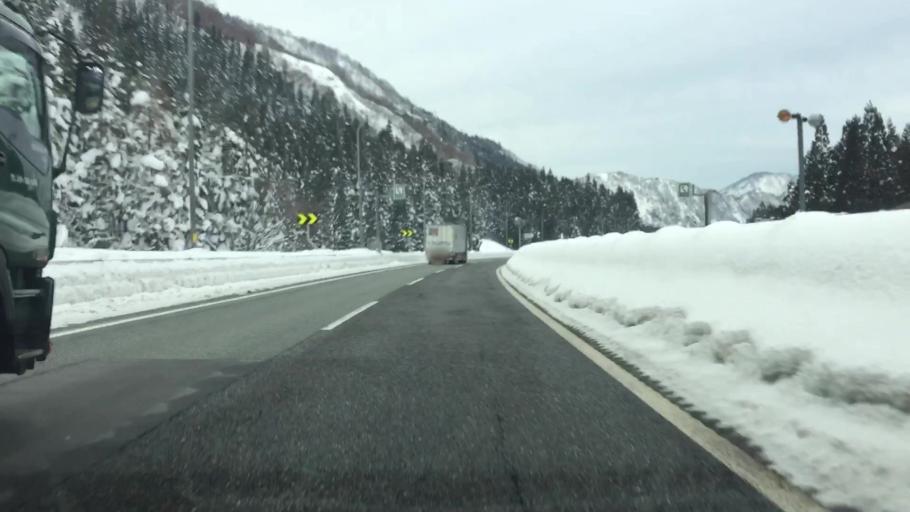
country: JP
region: Niigata
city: Shiozawa
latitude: 36.8865
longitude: 138.8499
